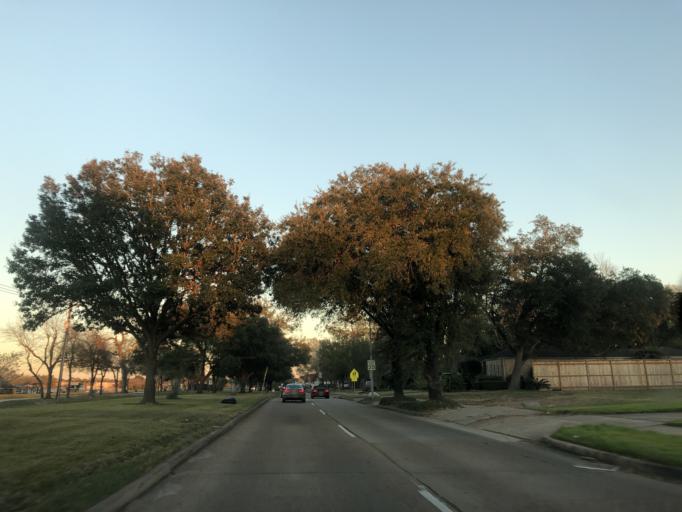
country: US
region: Texas
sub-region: Harris County
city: Bellaire
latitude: 29.6752
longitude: -95.4824
